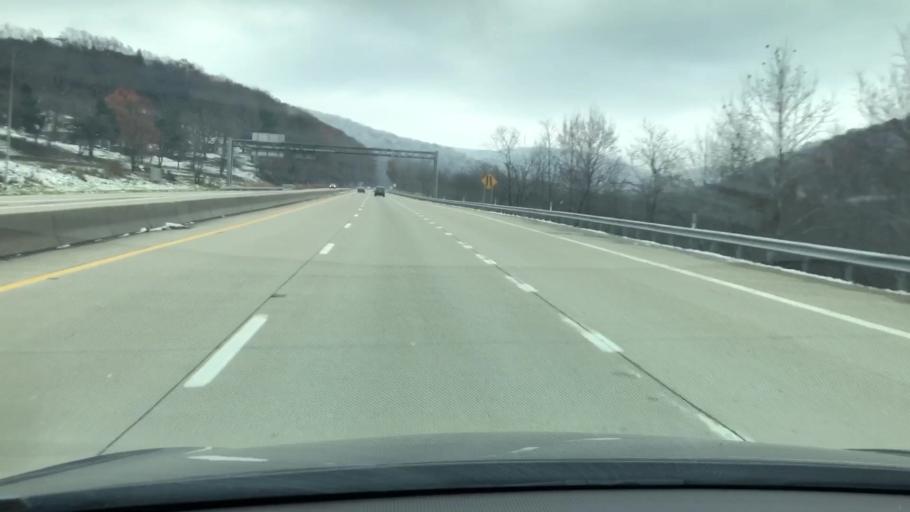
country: US
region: Pennsylvania
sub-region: Fayette County
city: Hopwood
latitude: 39.8678
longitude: -79.6924
